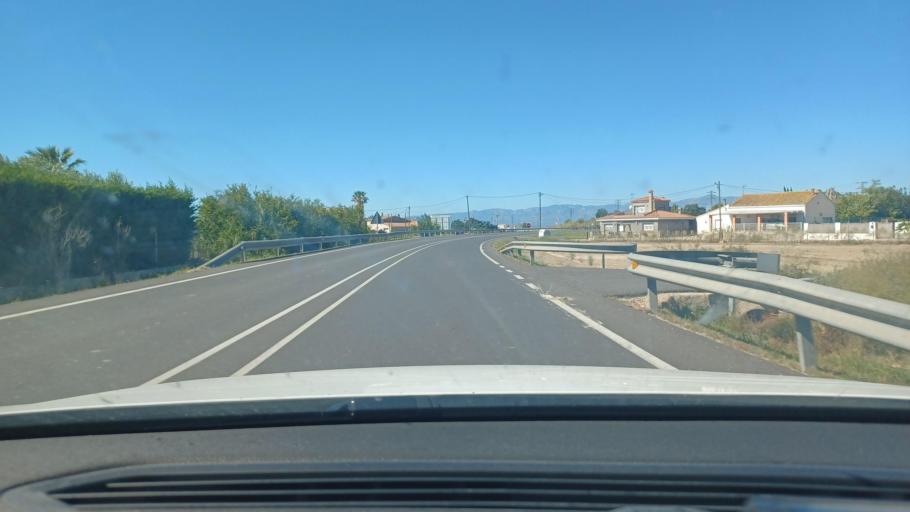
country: ES
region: Catalonia
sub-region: Provincia de Tarragona
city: Deltebre
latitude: 40.7261
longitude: 0.6747
